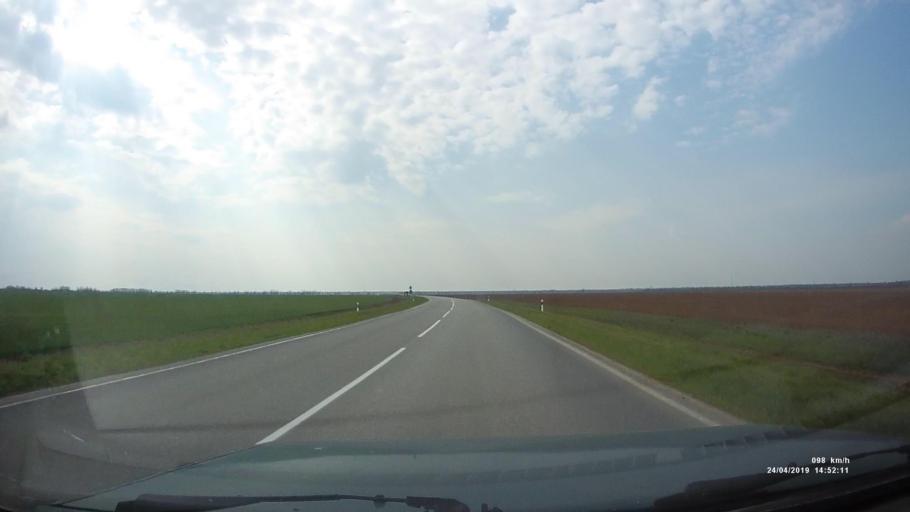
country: RU
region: Rostov
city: Remontnoye
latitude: 46.5297
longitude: 43.6861
